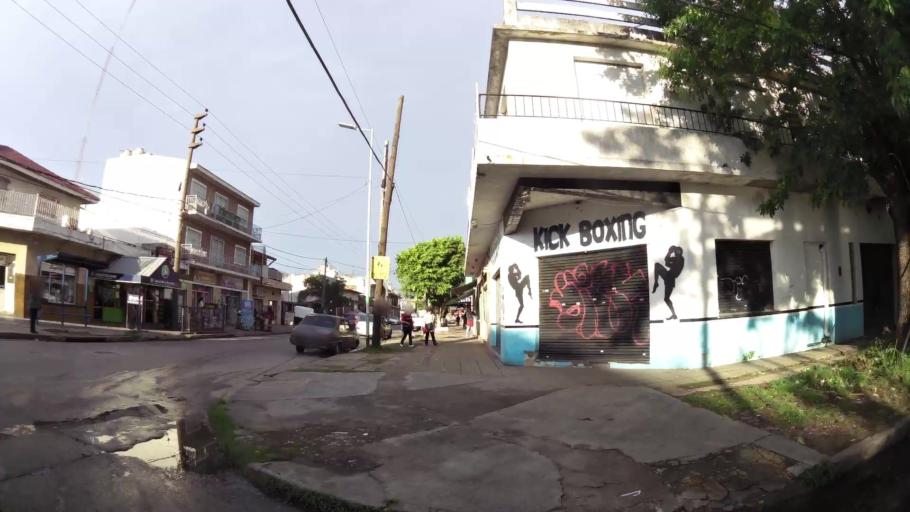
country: AR
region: Buenos Aires
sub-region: Partido de Lomas de Zamora
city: Lomas de Zamora
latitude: -34.7430
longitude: -58.3512
